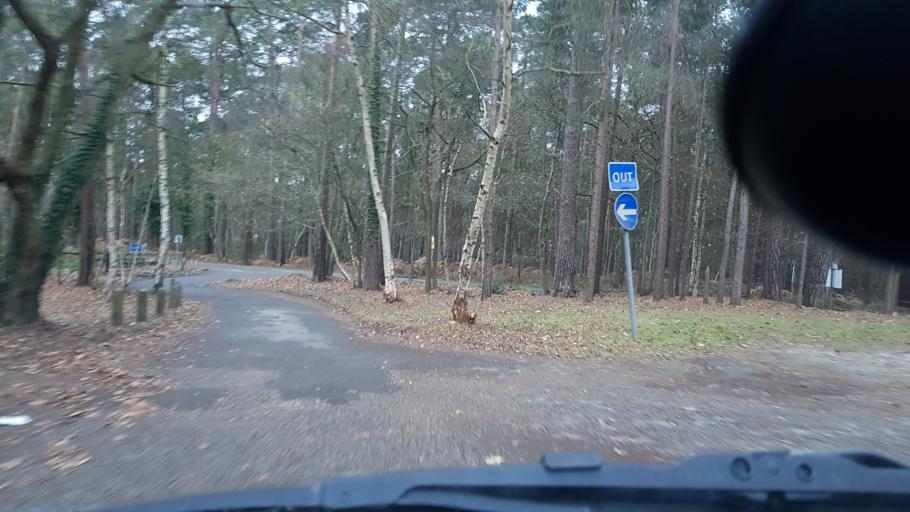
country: GB
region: England
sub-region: Surrey
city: Byfleet
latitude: 51.3166
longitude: -0.4535
